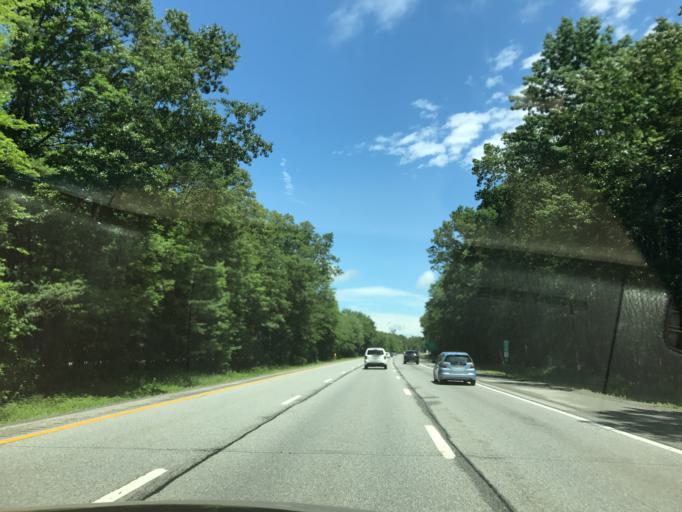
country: US
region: New York
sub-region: Saratoga County
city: Saratoga Springs
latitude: 43.1515
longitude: -73.7247
